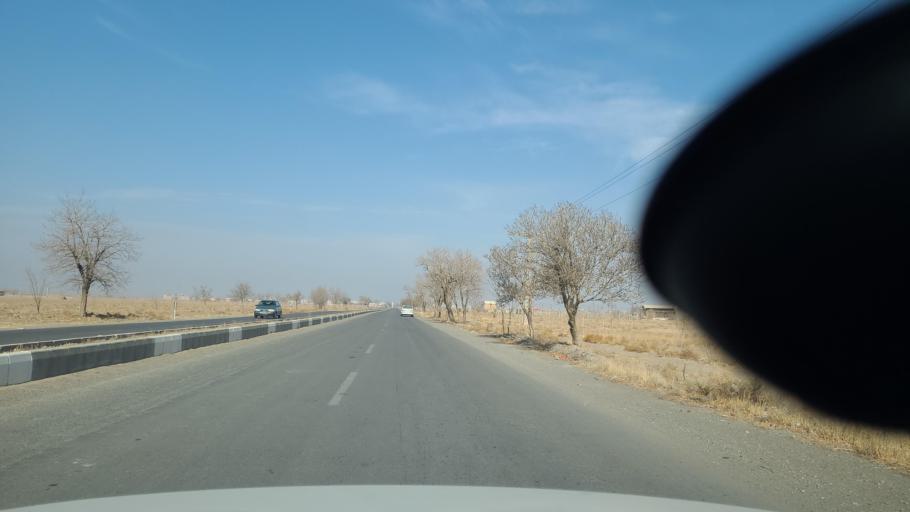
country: IR
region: Razavi Khorasan
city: Fariman
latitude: 35.6655
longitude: 59.8417
